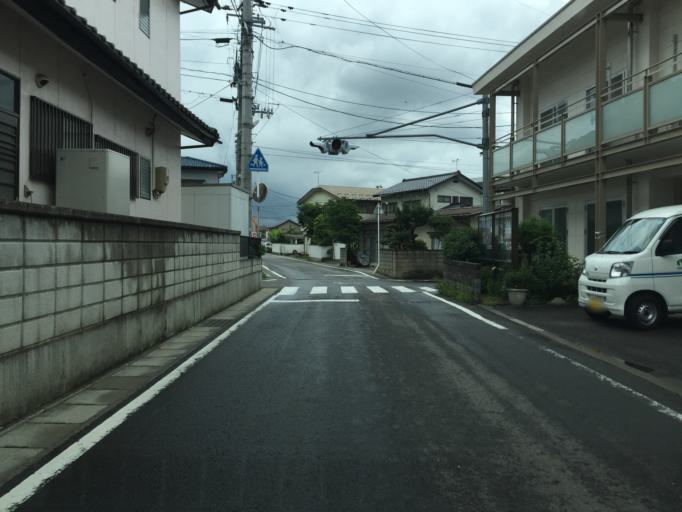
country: JP
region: Fukushima
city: Fukushima-shi
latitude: 37.7438
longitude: 140.4770
